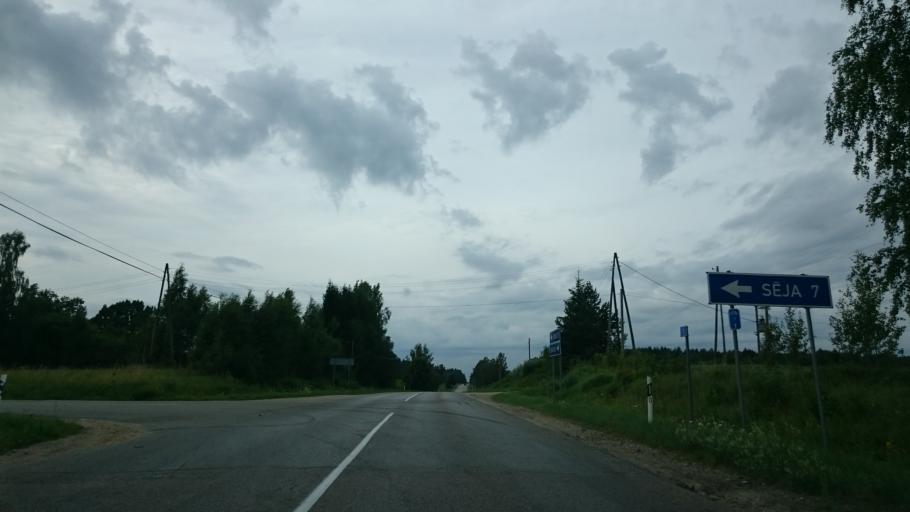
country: LV
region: Krimulda
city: Ragana
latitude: 57.1879
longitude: 24.7092
